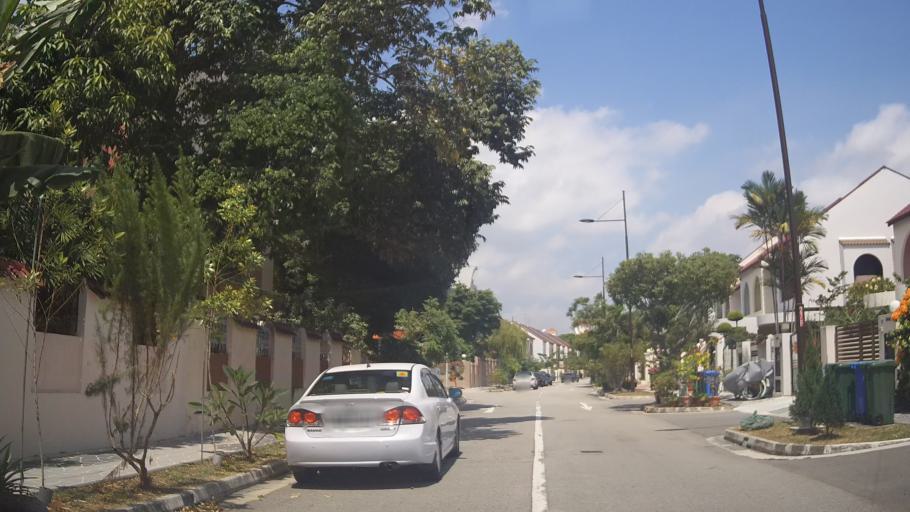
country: SG
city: Singapore
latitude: 1.3257
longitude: 103.9542
